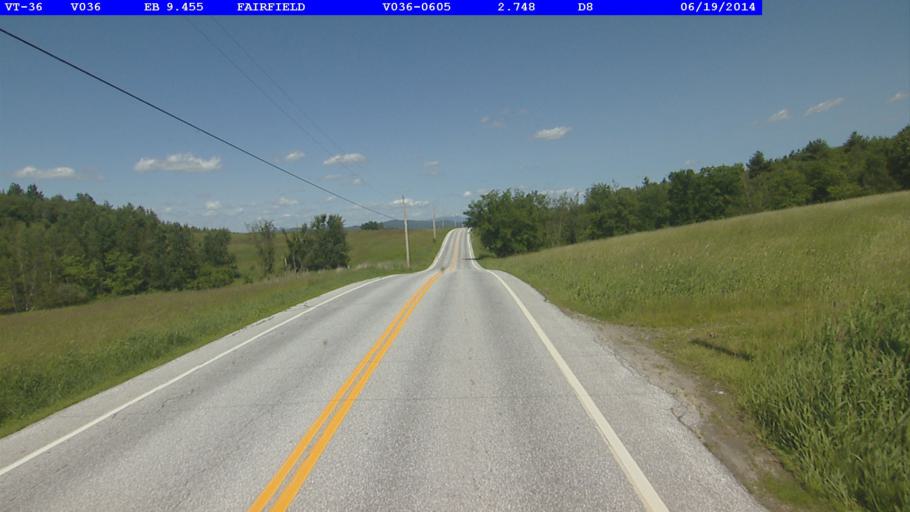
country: US
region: Vermont
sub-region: Franklin County
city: Saint Albans
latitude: 44.7928
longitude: -72.9778
